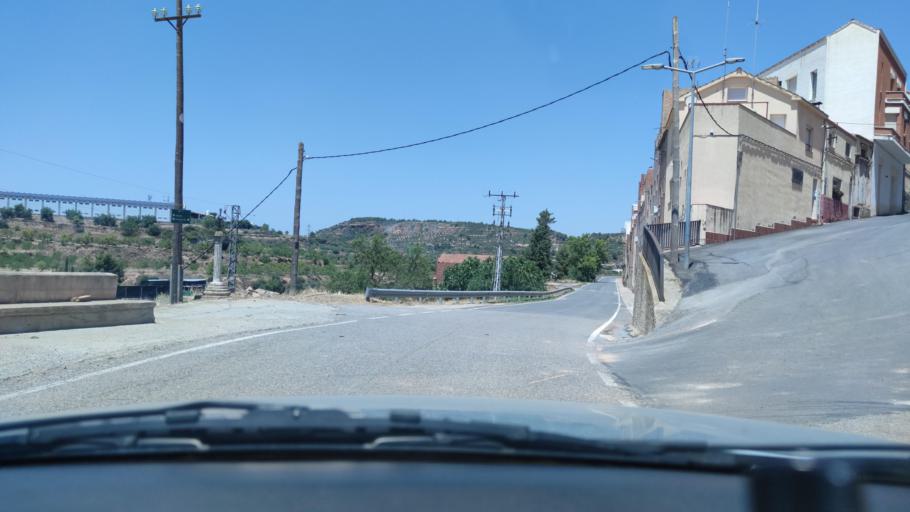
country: ES
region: Catalonia
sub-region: Provincia de Lleida
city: Juncosa
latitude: 41.3701
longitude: 0.7746
